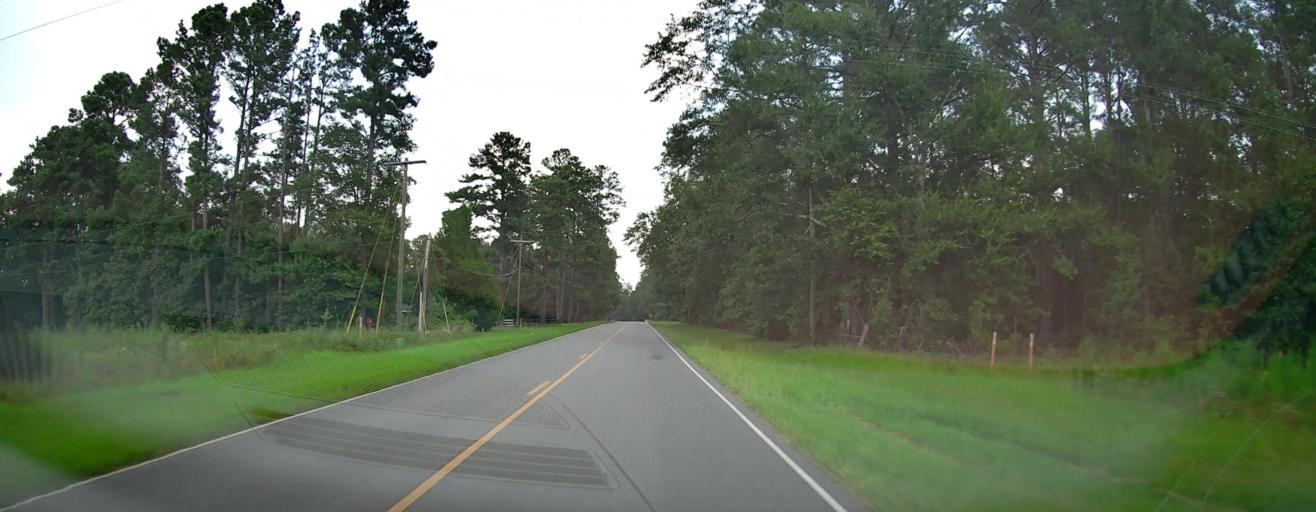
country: US
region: Georgia
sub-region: Laurens County
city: Dublin
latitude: 32.5759
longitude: -82.9064
